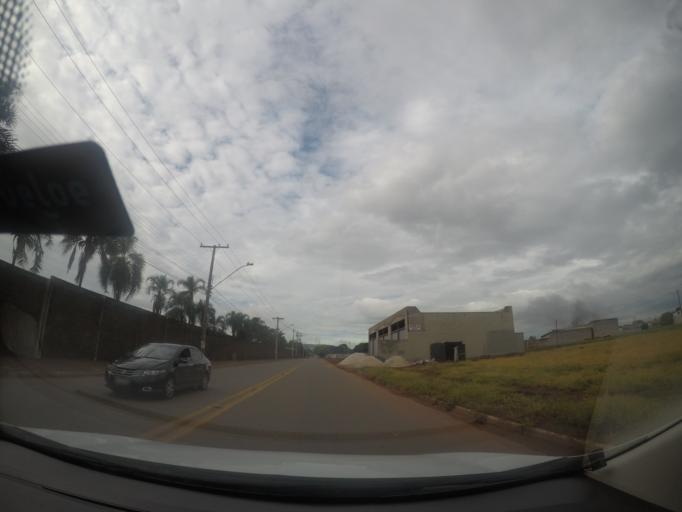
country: BR
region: Goias
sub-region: Goiania
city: Goiania
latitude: -16.6328
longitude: -49.3292
